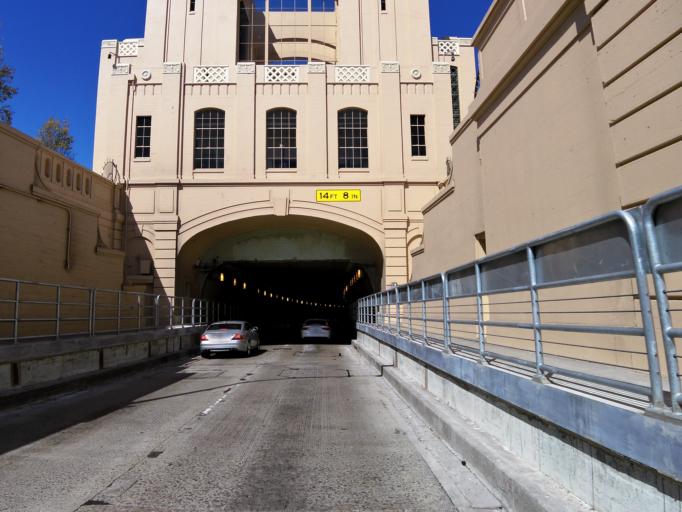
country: US
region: California
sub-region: Alameda County
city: Oakland
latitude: 37.7872
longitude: -122.2766
